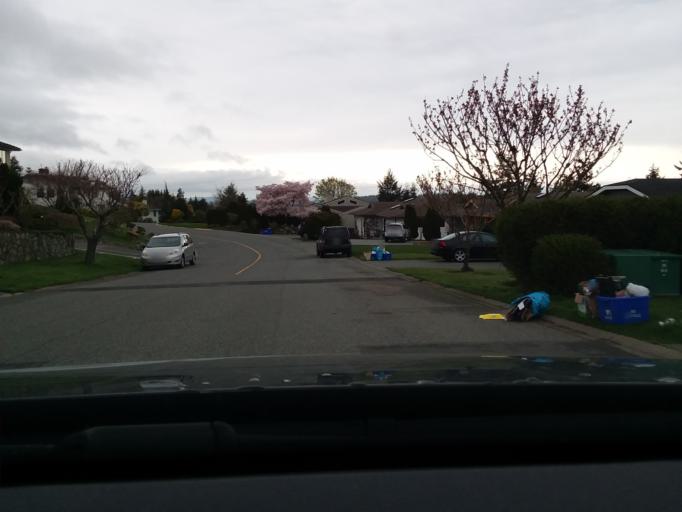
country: CA
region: British Columbia
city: North Saanich
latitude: 48.5610
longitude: -123.3974
